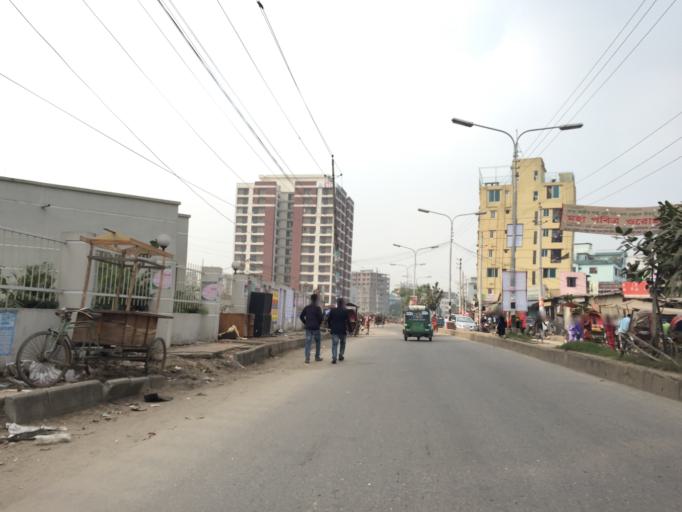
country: BD
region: Dhaka
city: Azimpur
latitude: 23.7776
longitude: 90.3703
